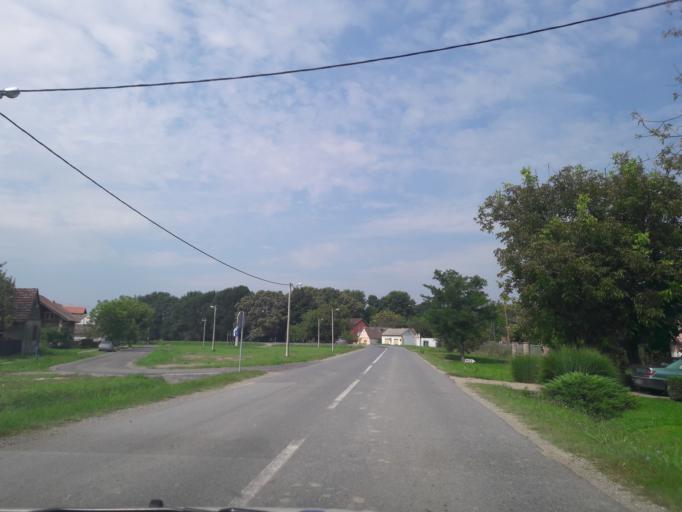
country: HR
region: Osjecko-Baranjska
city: Bizovac
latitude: 45.5148
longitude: 18.4746
